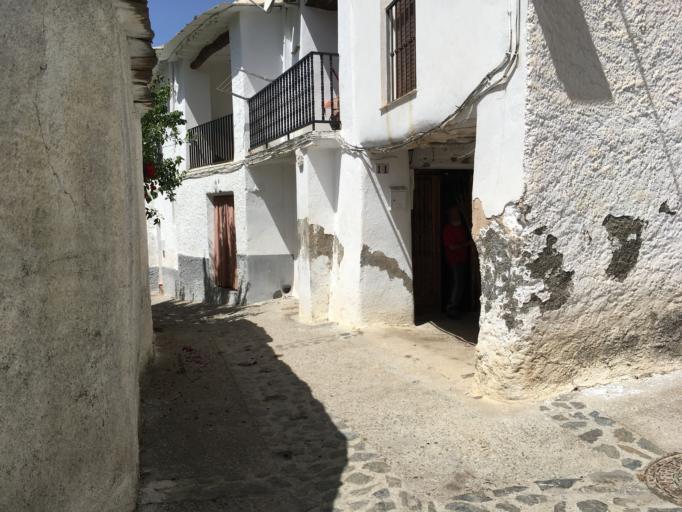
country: ES
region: Andalusia
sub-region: Provincia de Granada
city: Portugos
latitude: 36.9302
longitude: -3.3122
